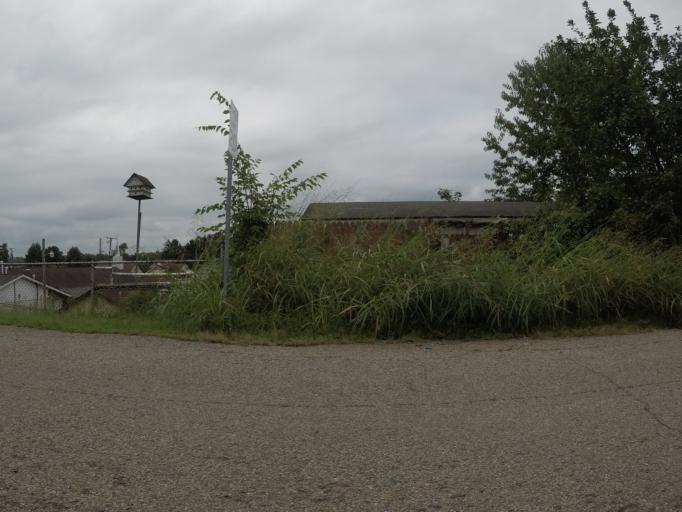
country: US
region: West Virginia
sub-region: Cabell County
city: Pea Ridge
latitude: 38.4282
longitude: -82.3758
